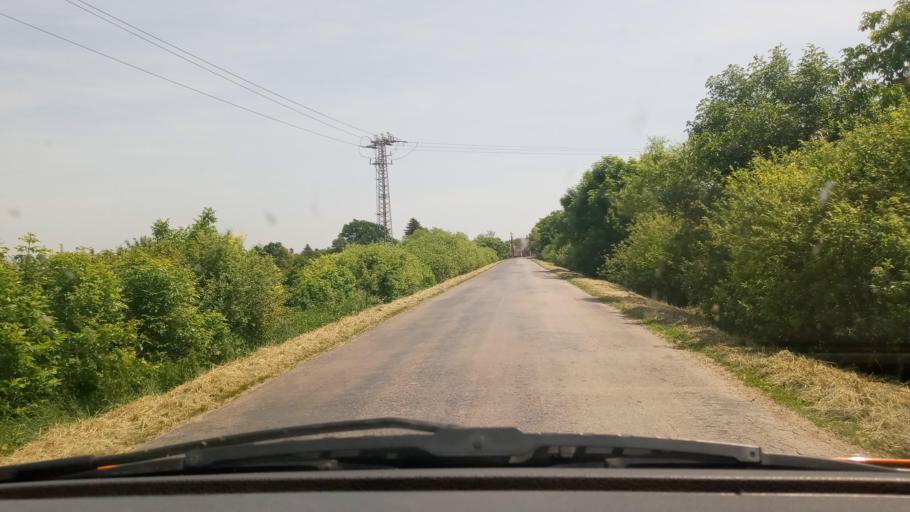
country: HU
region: Baranya
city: Szigetvar
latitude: 45.9653
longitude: 17.7063
